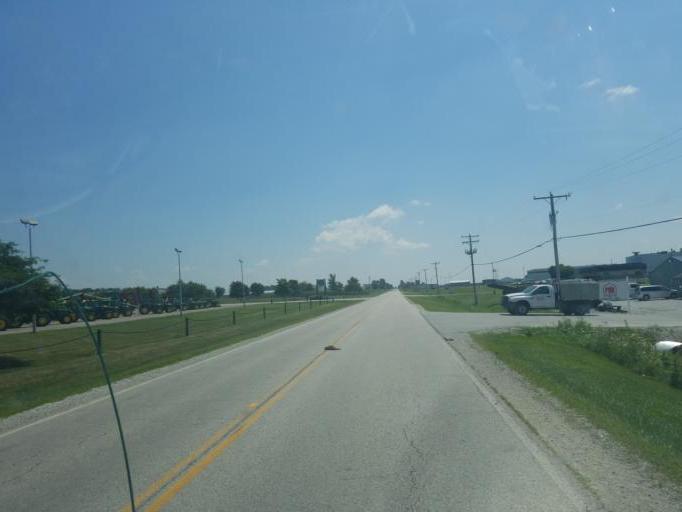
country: US
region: Ohio
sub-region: Shelby County
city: Botkins
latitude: 40.4353
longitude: -84.1781
